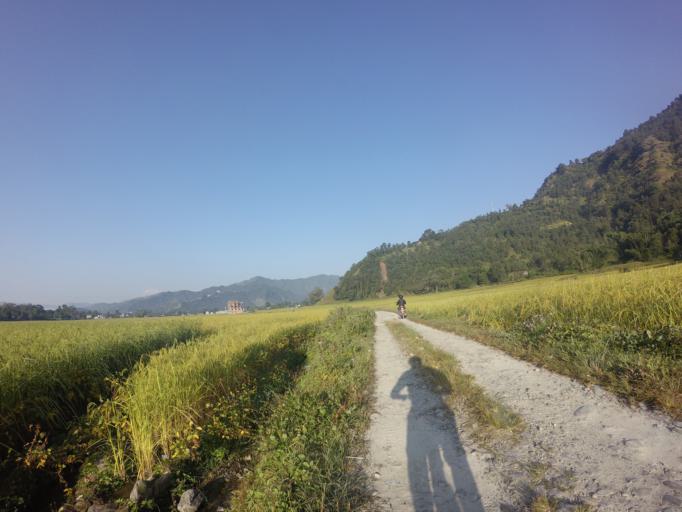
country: NP
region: Western Region
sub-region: Gandaki Zone
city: Pokhara
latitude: 28.2505
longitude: 84.0040
